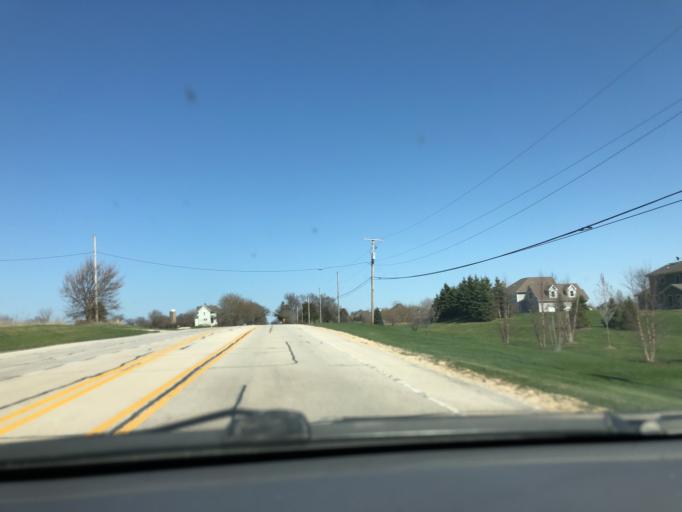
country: US
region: Illinois
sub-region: Kane County
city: Hampshire
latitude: 42.1609
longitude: -88.5039
